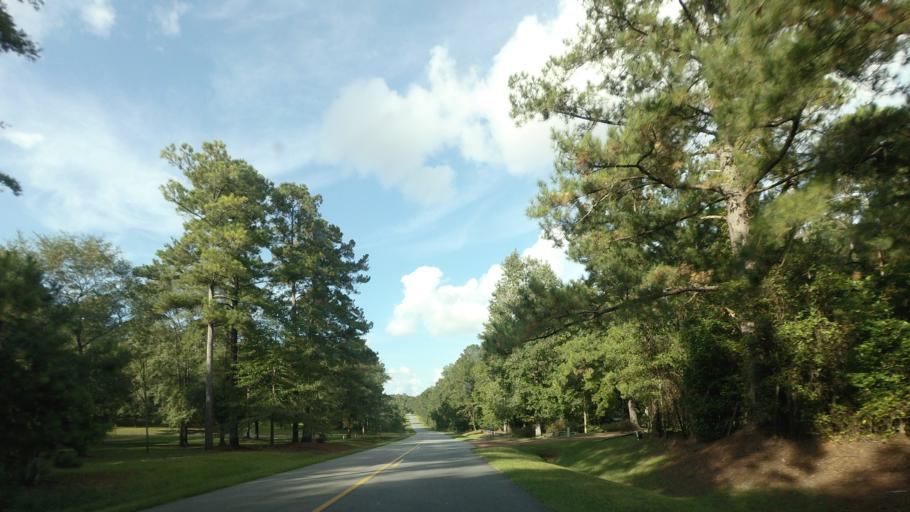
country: US
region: Georgia
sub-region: Pulaski County
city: Hawkinsville
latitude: 32.2900
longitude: -83.4937
